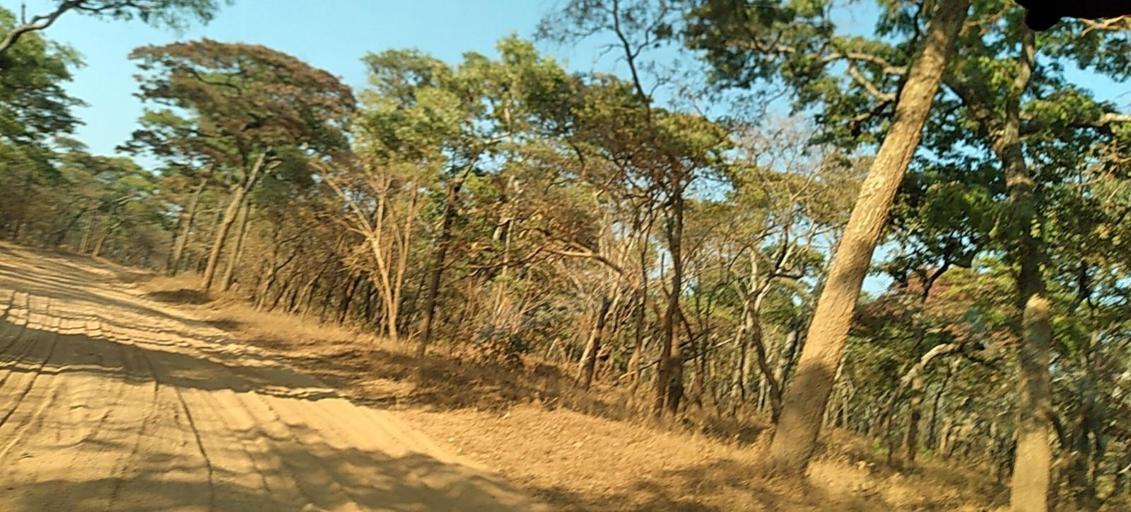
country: ZM
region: North-Western
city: Kasempa
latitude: -13.5646
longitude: 25.9970
